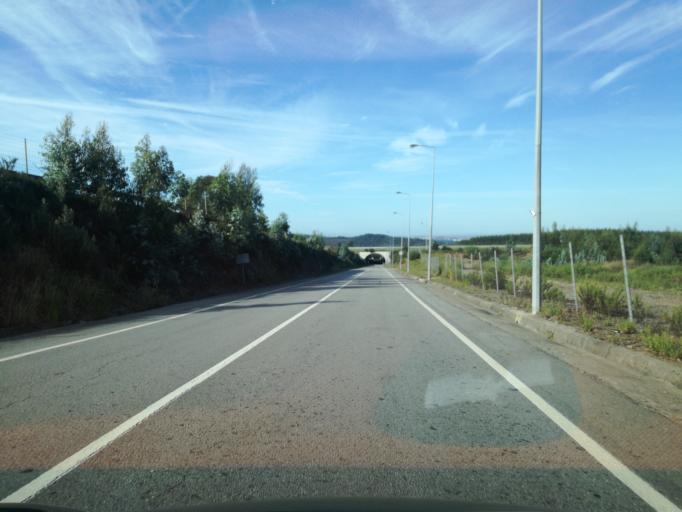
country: PT
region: Porto
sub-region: Trofa
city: Sao Romao do Coronado
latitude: 41.2854
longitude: -8.5162
